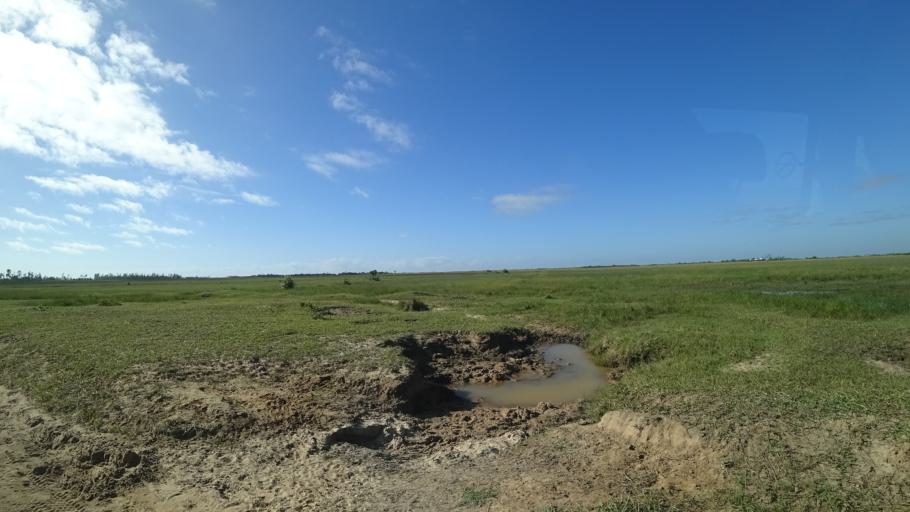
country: MZ
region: Sofala
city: Beira
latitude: -19.7280
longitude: 34.9865
